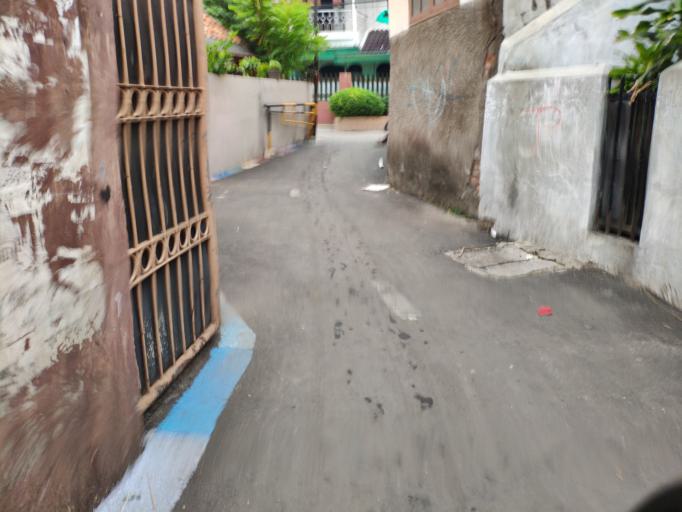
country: ID
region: Jakarta Raya
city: Jakarta
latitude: -6.1981
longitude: 106.8667
